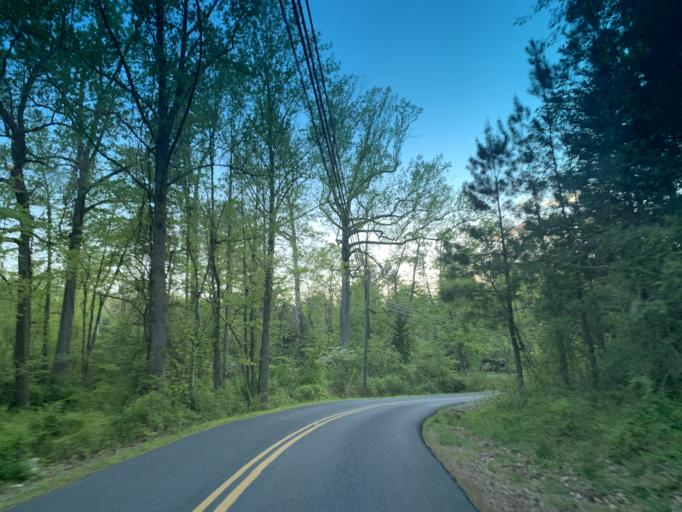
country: US
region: Maryland
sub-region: Harford County
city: Riverside
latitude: 39.5247
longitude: -76.2536
